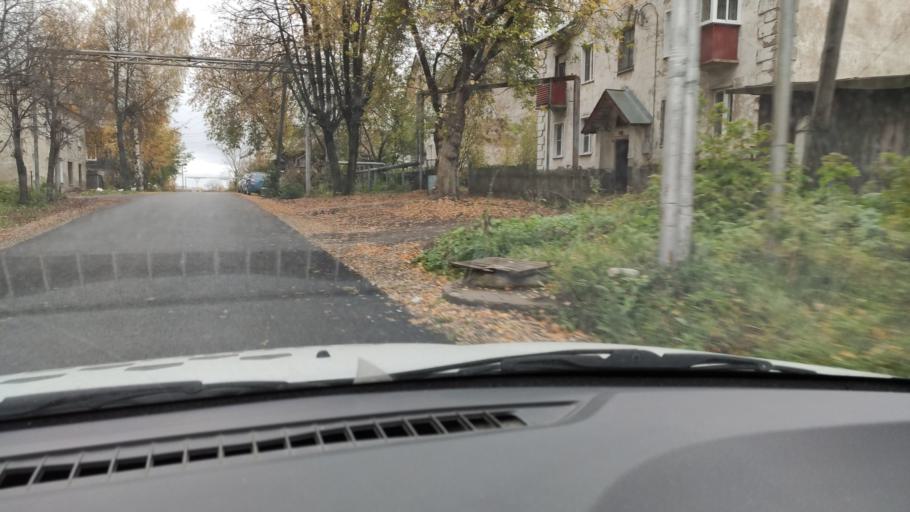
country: RU
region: Kirov
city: Slobodskoy
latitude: 58.7386
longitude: 50.1837
